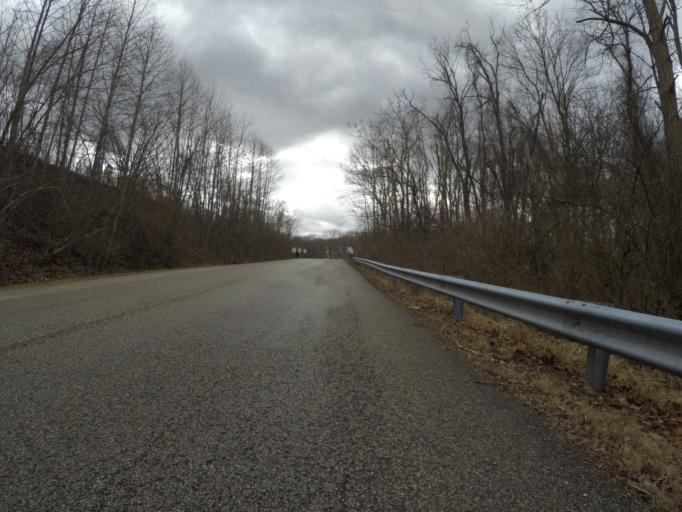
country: US
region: West Virginia
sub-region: Cabell County
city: Pea Ridge
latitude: 38.4032
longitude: -82.3739
